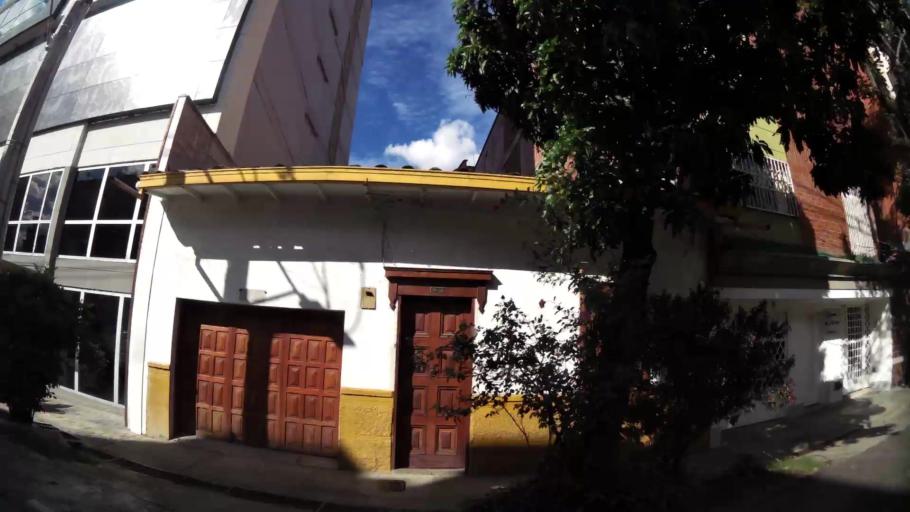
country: CO
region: Antioquia
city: Envigado
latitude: 6.1722
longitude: -75.5919
